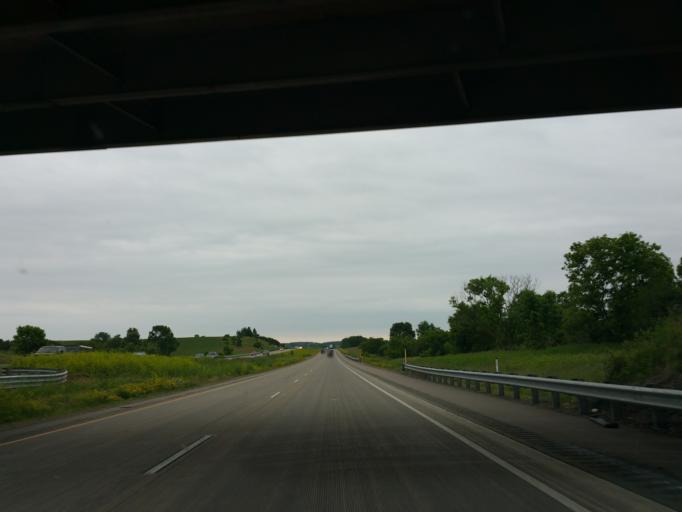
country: US
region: Wisconsin
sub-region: Eau Claire County
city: Fall Creek
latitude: 44.6616
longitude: -91.3154
